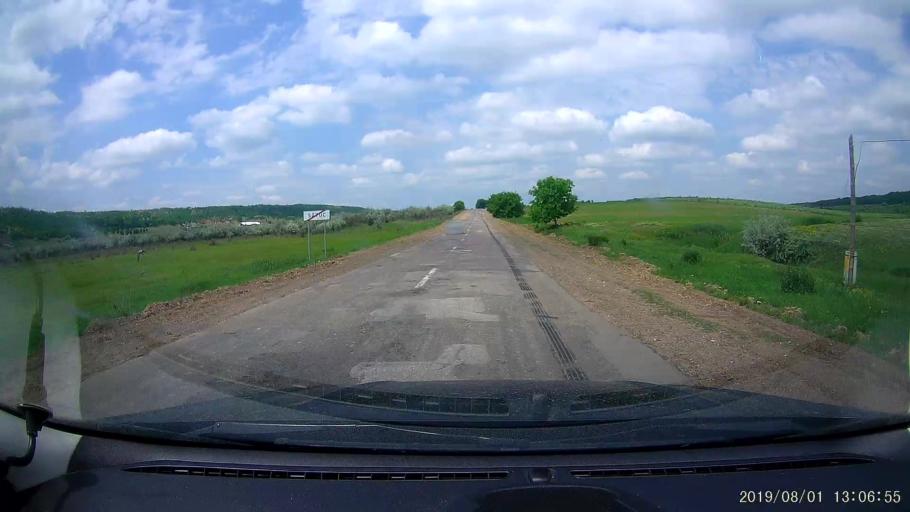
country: MD
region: Gagauzia
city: Vulcanesti
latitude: 45.8045
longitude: 28.3491
